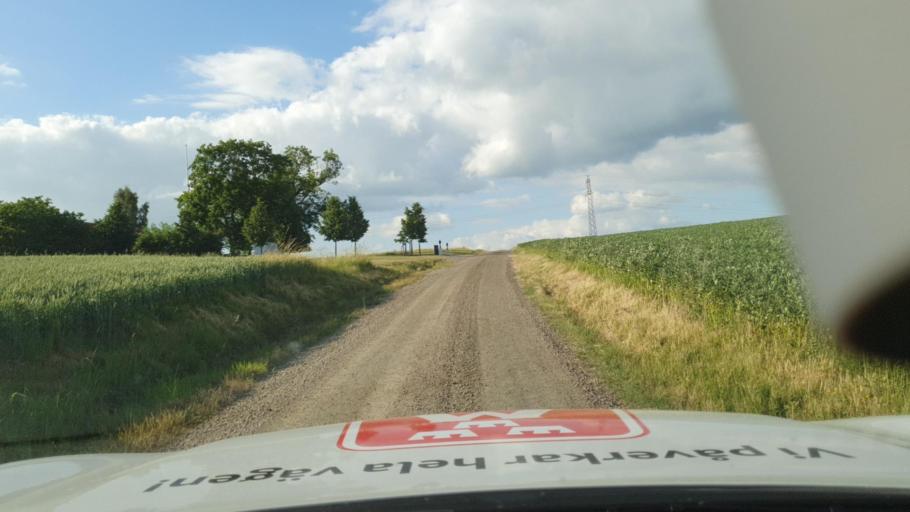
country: SE
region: Skane
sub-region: Skurups Kommun
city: Rydsgard
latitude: 55.4998
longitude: 13.5769
